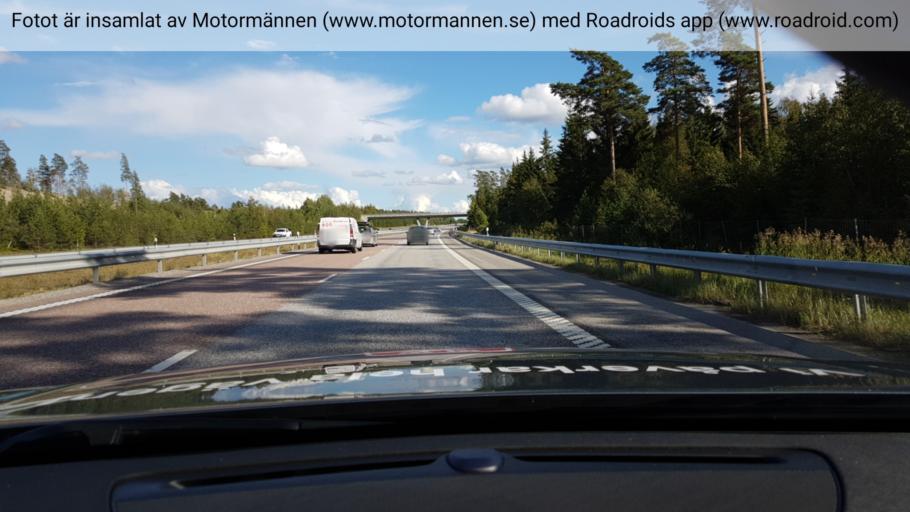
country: SE
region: Soedermanland
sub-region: Strangnas Kommun
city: Mariefred
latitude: 59.2146
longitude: 17.3154
